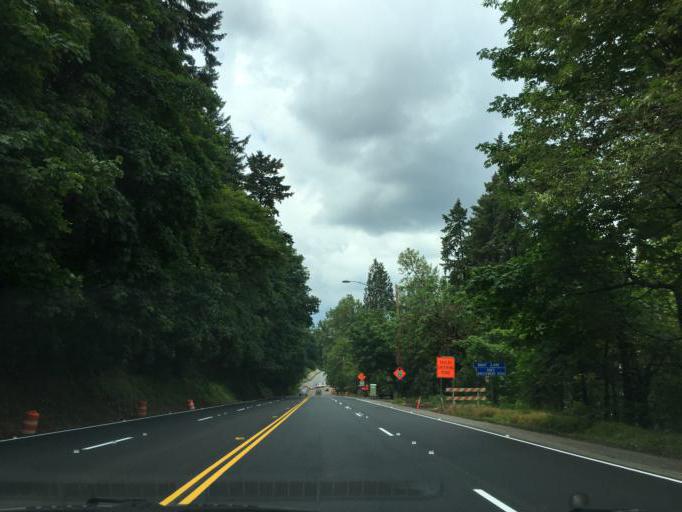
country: US
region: Oregon
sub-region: Clackamas County
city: Milwaukie
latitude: 45.4586
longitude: -122.6654
